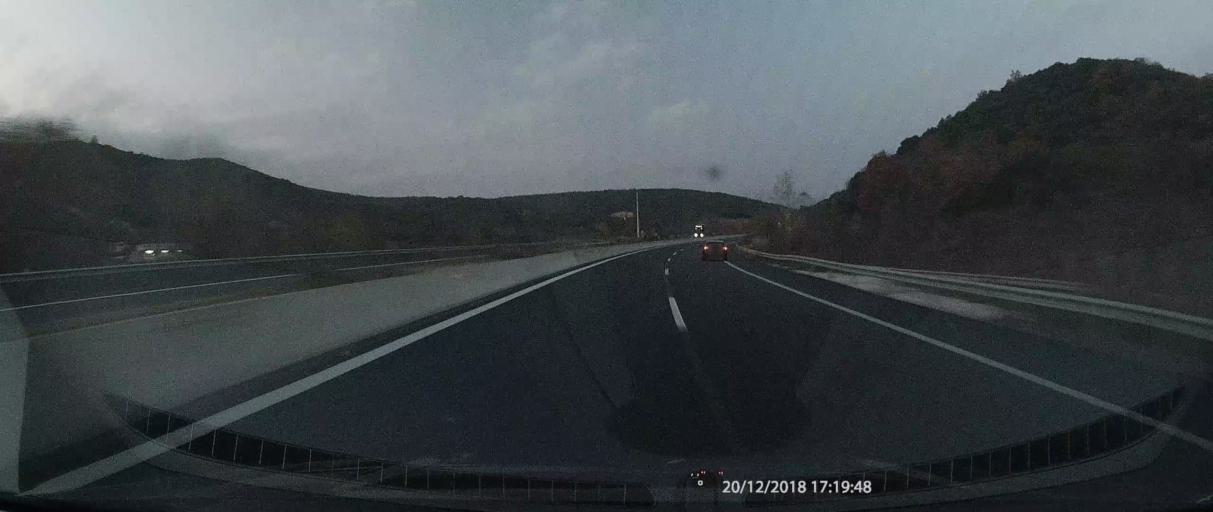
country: GR
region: Thessaly
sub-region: Nomos Larisis
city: Pyrgetos
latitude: 39.9522
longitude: 22.6463
